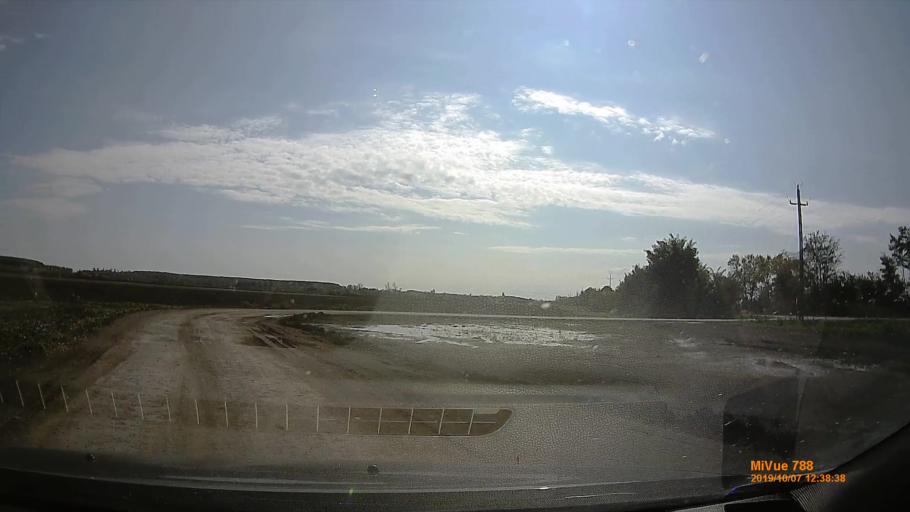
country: HU
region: Jasz-Nagykun-Szolnok
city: Kunszentmarton
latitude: 46.8667
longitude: 20.2661
